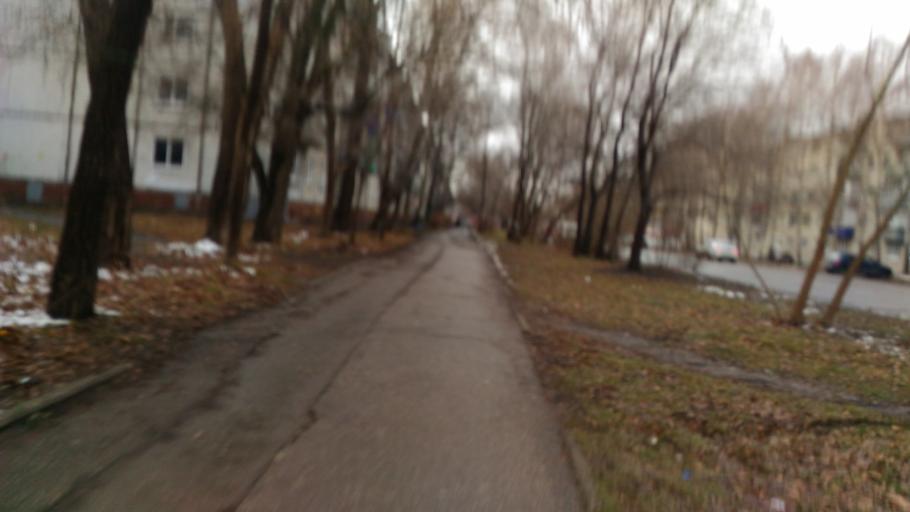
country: RU
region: Ulyanovsk
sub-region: Ulyanovskiy Rayon
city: Ulyanovsk
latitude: 54.3477
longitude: 48.3896
